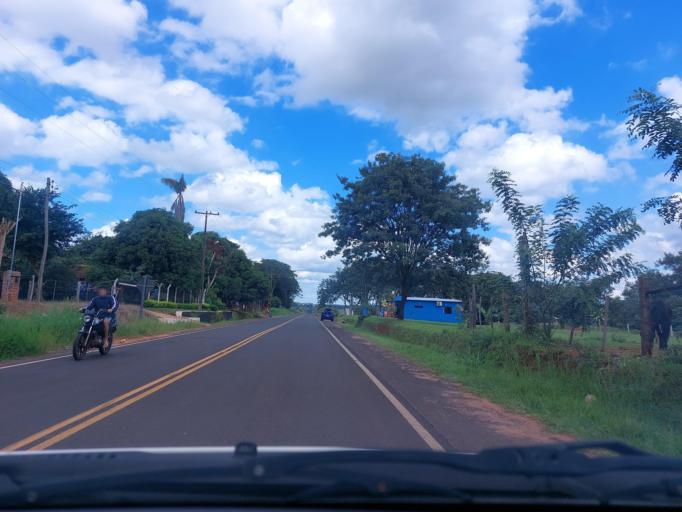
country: PY
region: San Pedro
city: Guayaybi
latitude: -24.5323
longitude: -56.5197
